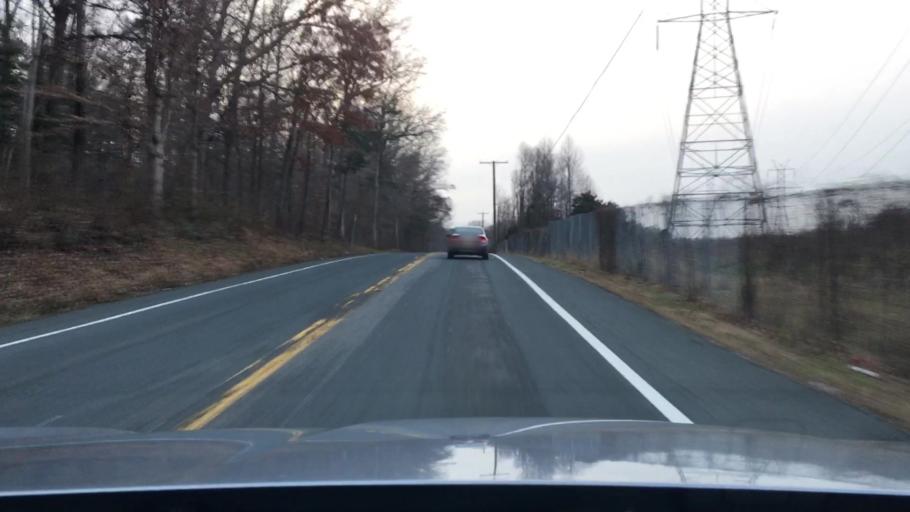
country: US
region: Maryland
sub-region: Anne Arundel County
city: Maryland City
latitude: 39.0454
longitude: -76.8025
